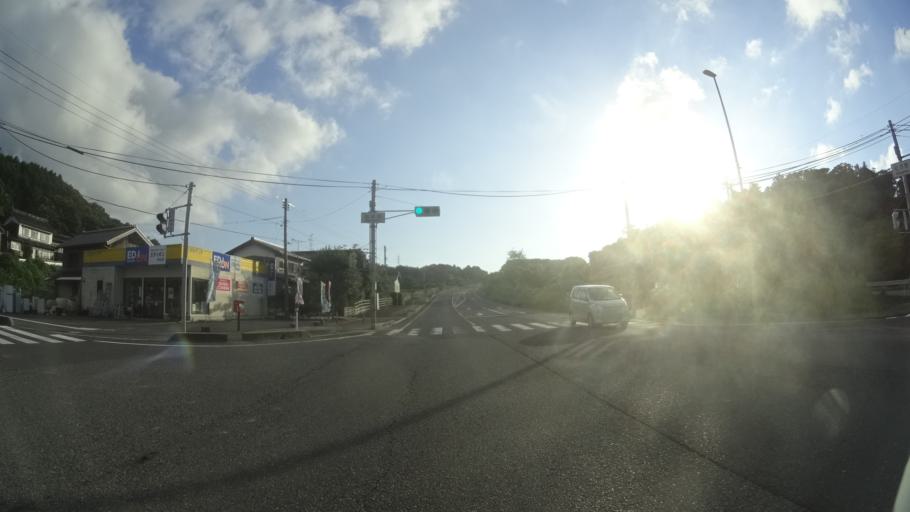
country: JP
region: Tottori
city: Yonago
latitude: 35.5181
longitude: 133.5535
